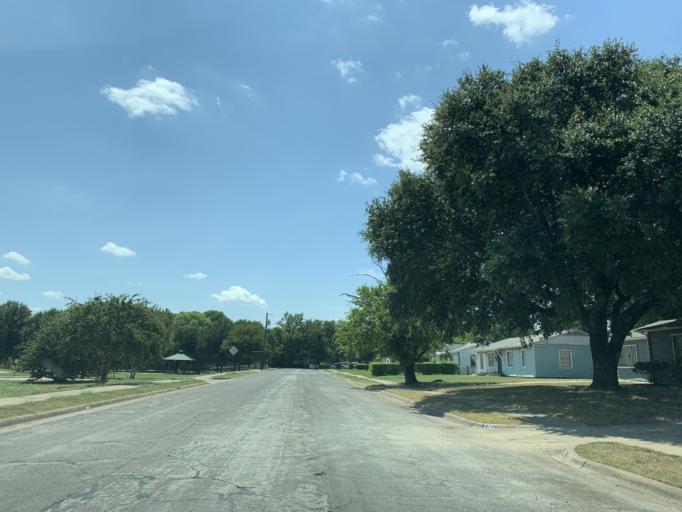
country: US
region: Texas
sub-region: Dallas County
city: Hutchins
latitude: 32.6822
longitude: -96.7812
